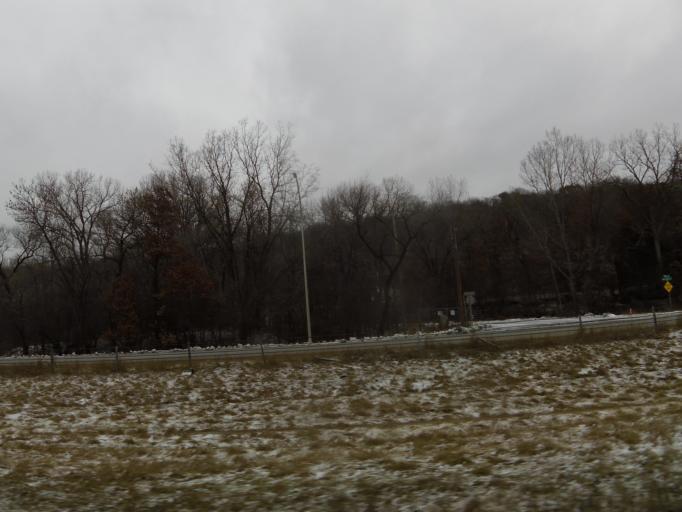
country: US
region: Minnesota
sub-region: Ramsey County
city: Maplewood
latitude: 44.9368
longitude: -93.0312
